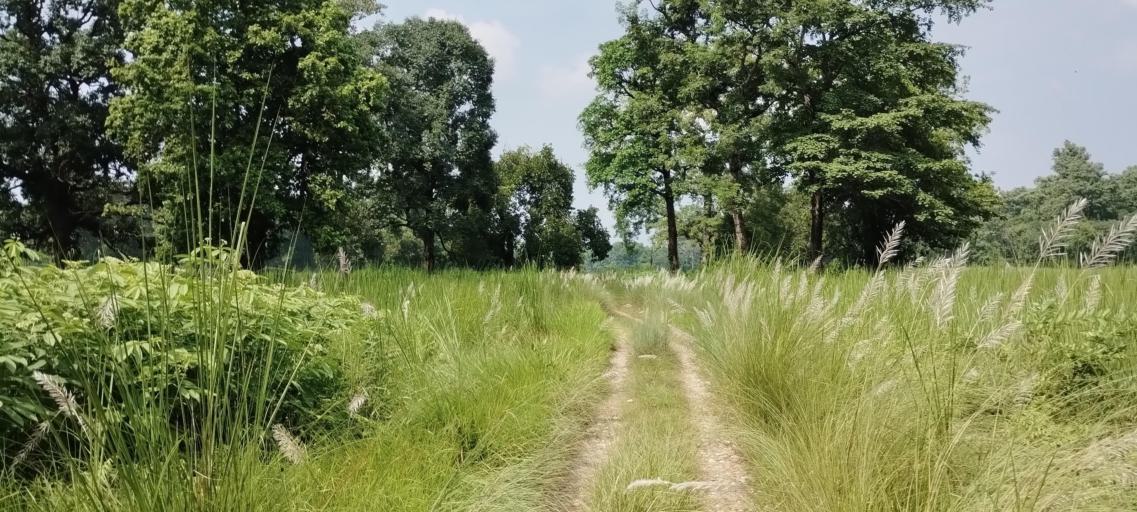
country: NP
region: Far Western
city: Tikapur
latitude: 28.5075
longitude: 81.2515
